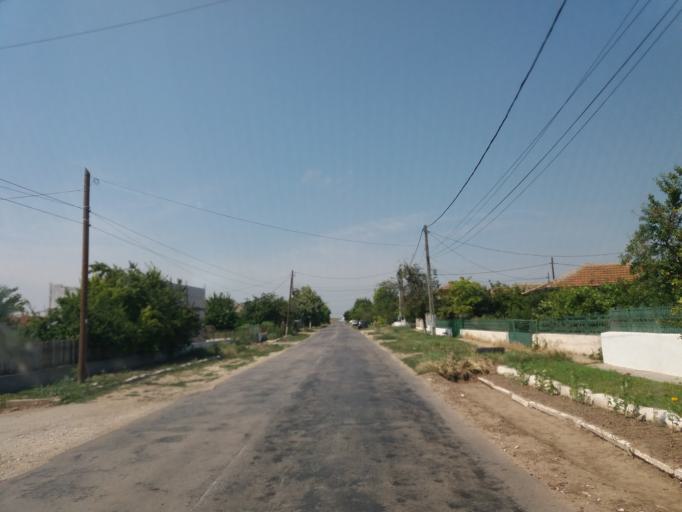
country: RO
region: Constanta
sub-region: Comuna Corbu
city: Corbu
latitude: 44.4206
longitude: 28.6607
